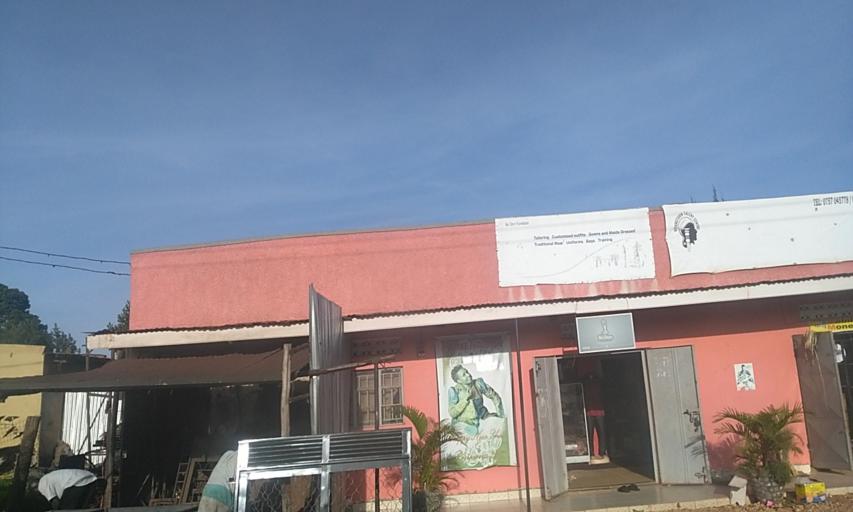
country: UG
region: Central Region
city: Kampala Central Division
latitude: 0.3672
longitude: 32.5975
